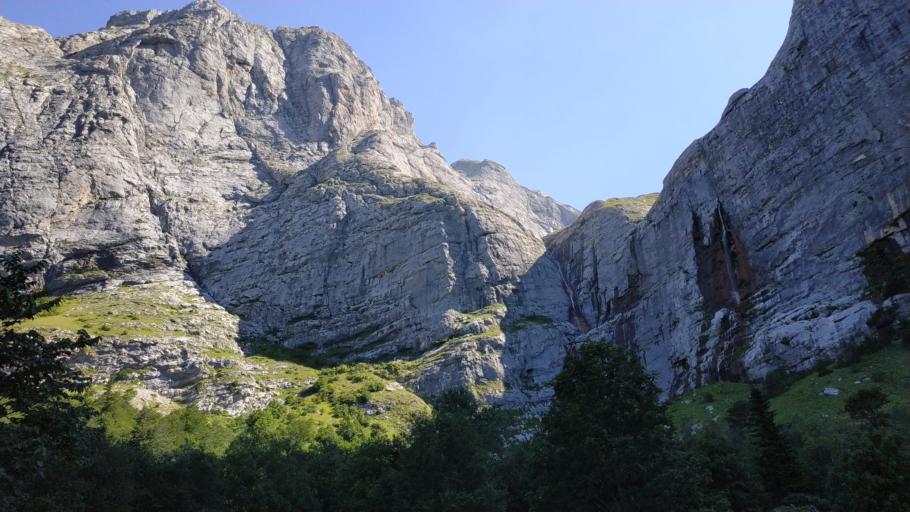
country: RU
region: Krasnodarskiy
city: Dagomys
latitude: 43.9782
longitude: 39.8775
